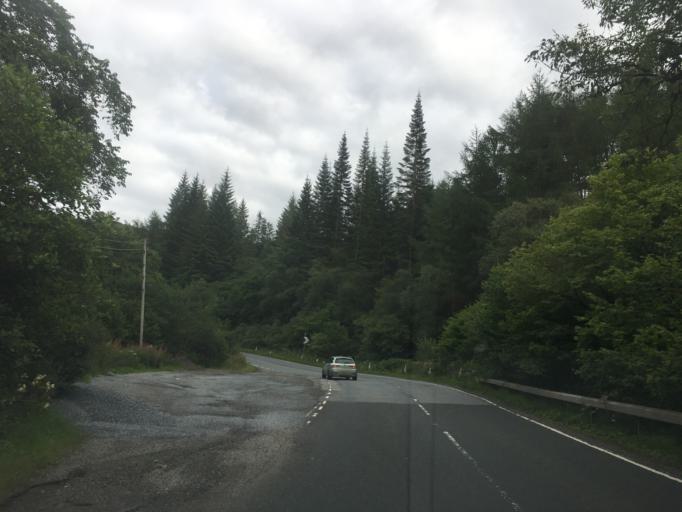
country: GB
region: Scotland
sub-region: Argyll and Bute
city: Oban
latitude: 56.3126
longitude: -5.4792
